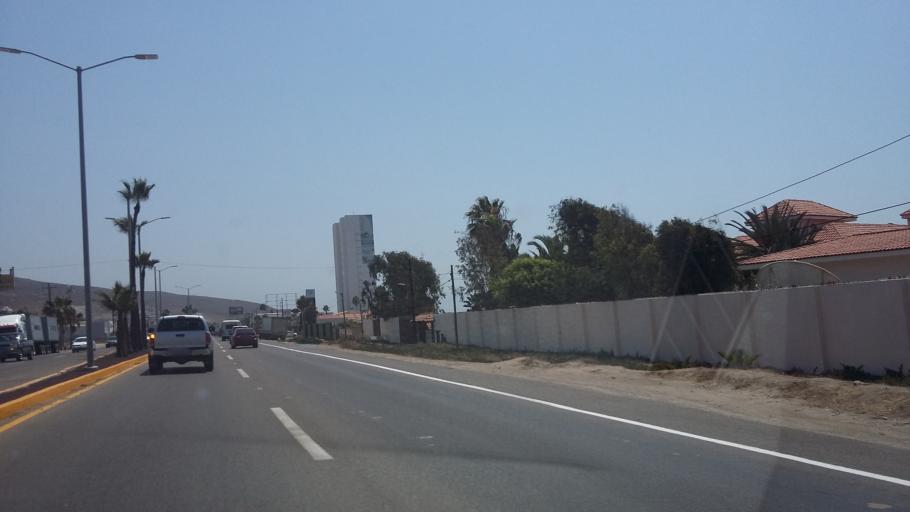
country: MX
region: Baja California
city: El Sauzal
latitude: 31.8909
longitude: -116.6932
